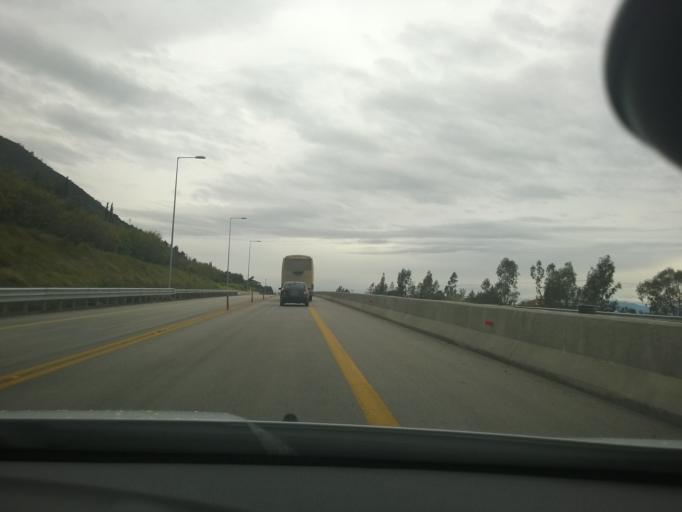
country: GR
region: West Greece
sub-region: Nomos Achaias
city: Temeni
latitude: 38.2107
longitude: 22.1273
